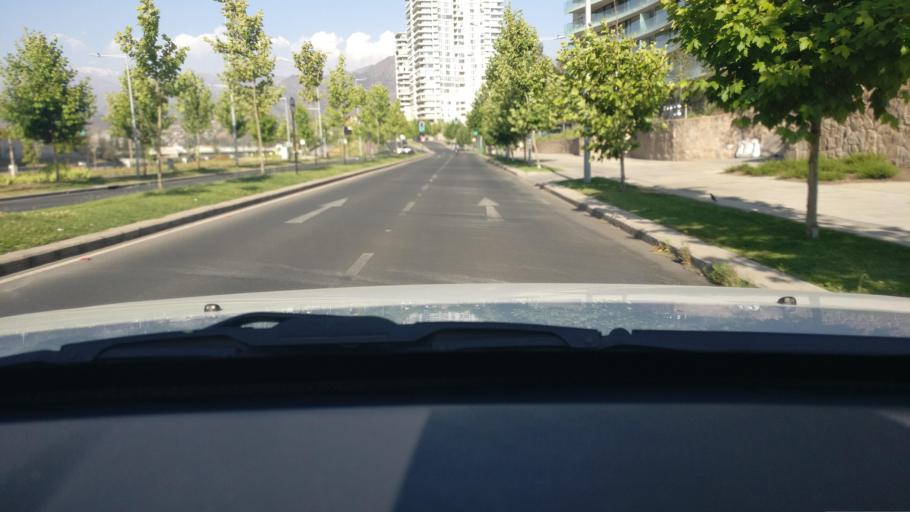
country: CL
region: Santiago Metropolitan
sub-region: Provincia de Santiago
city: Villa Presidente Frei, Nunoa, Santiago, Chile
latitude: -33.3728
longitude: -70.5230
